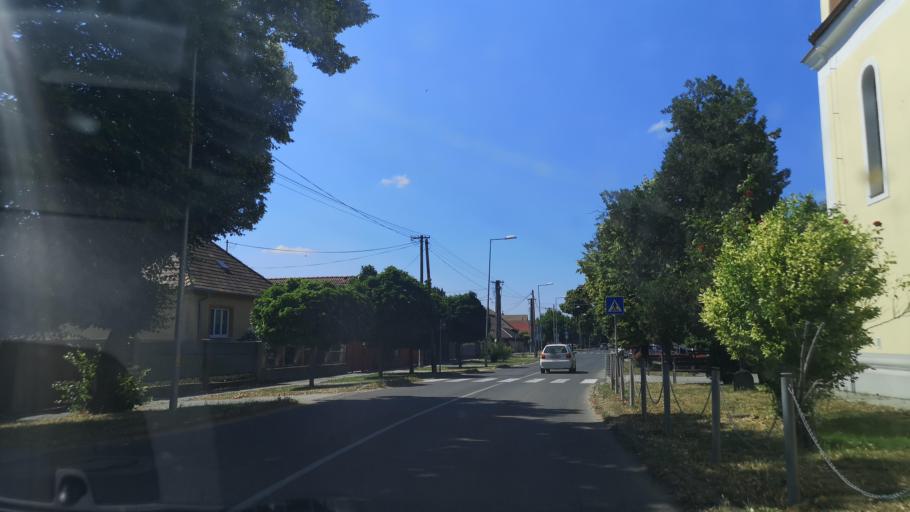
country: SK
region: Trnavsky
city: Samorin
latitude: 48.0533
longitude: 17.4600
